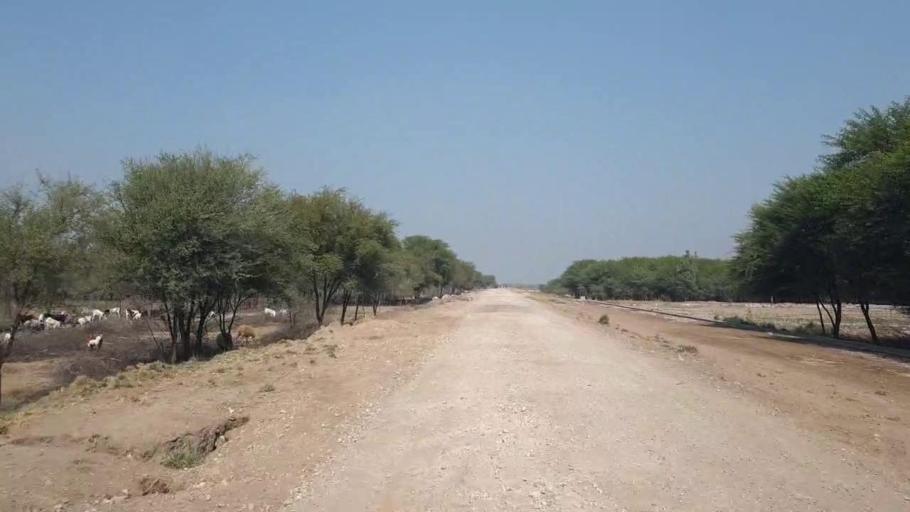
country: PK
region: Sindh
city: Mirwah Gorchani
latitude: 25.3583
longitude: 68.9316
